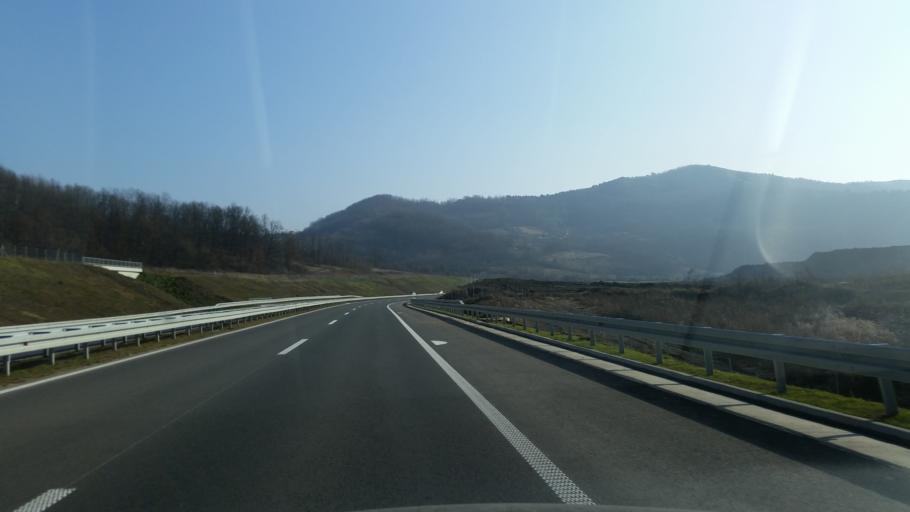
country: RS
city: Prislonica
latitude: 44.0015
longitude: 20.3989
